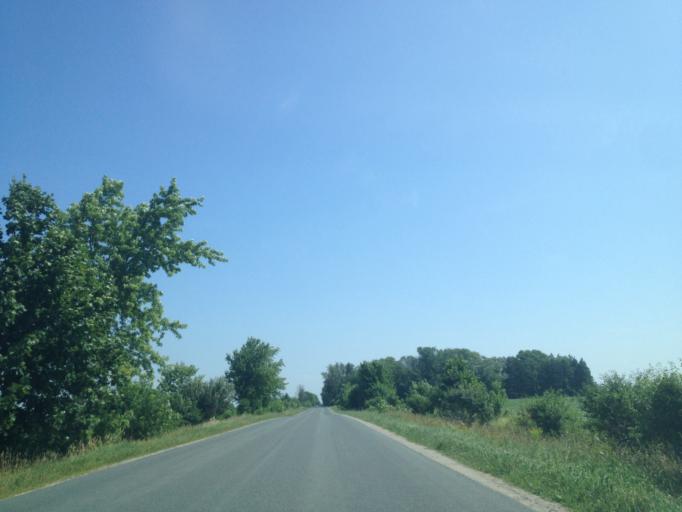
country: CA
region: Ontario
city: London
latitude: 43.2559
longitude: -81.2071
